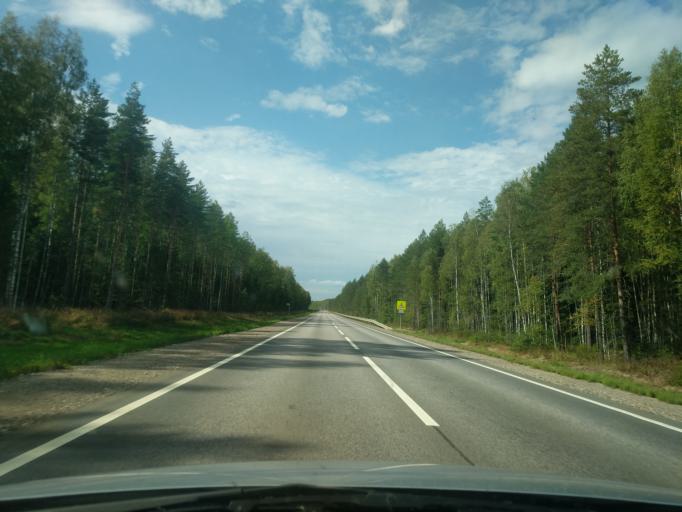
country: RU
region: Kostroma
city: Kadyy
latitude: 57.7996
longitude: 42.8208
